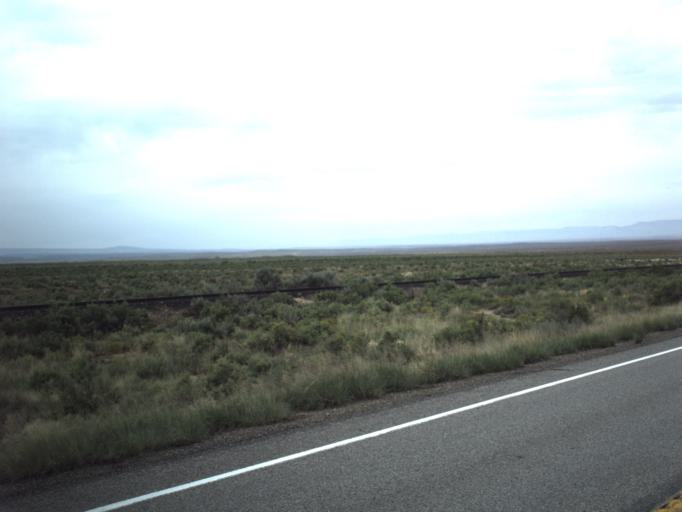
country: US
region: Utah
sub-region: Carbon County
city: East Carbon City
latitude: 39.5335
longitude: -110.5290
